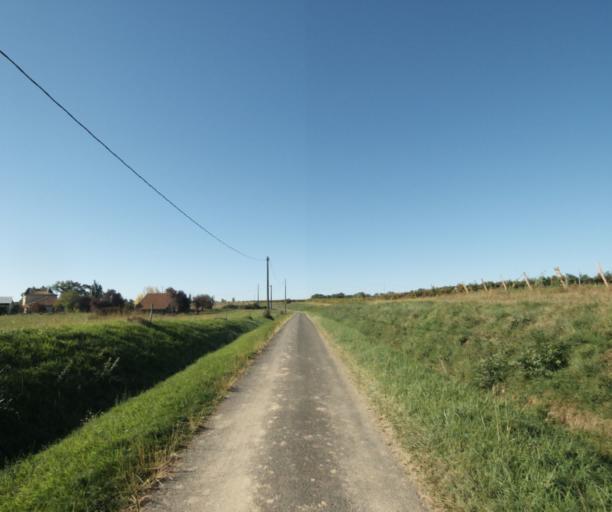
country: FR
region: Midi-Pyrenees
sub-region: Departement du Gers
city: Gondrin
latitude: 43.8206
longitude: 0.2360
